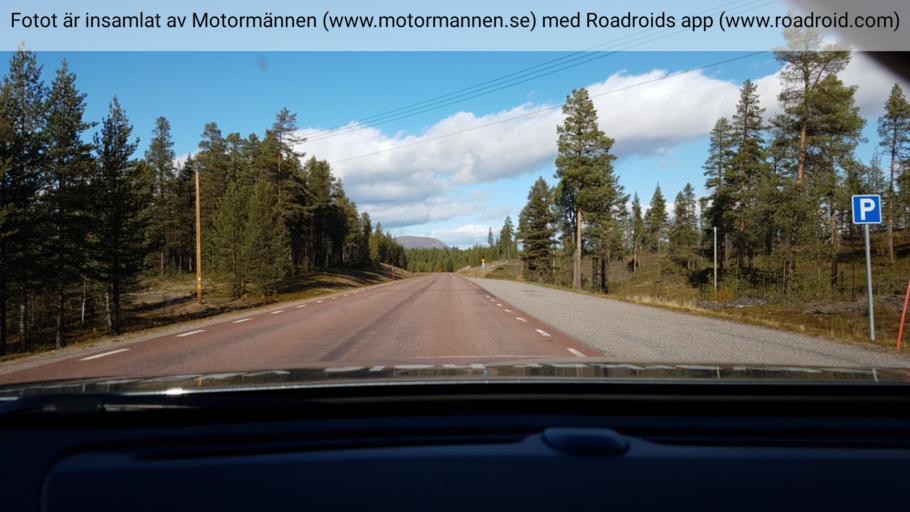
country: SE
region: Norrbotten
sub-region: Arjeplogs Kommun
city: Arjeplog
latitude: 66.0423
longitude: 18.0378
